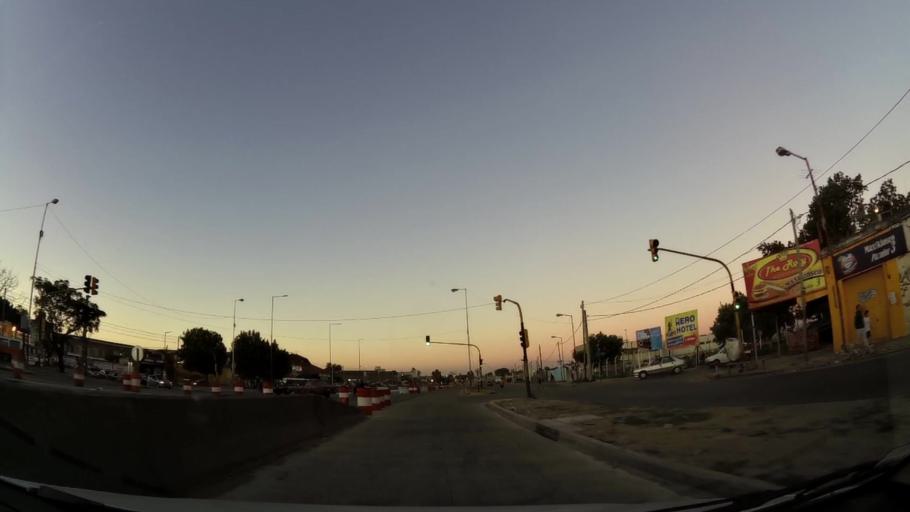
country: AR
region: Buenos Aires
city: San Justo
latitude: -34.7329
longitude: -58.6027
